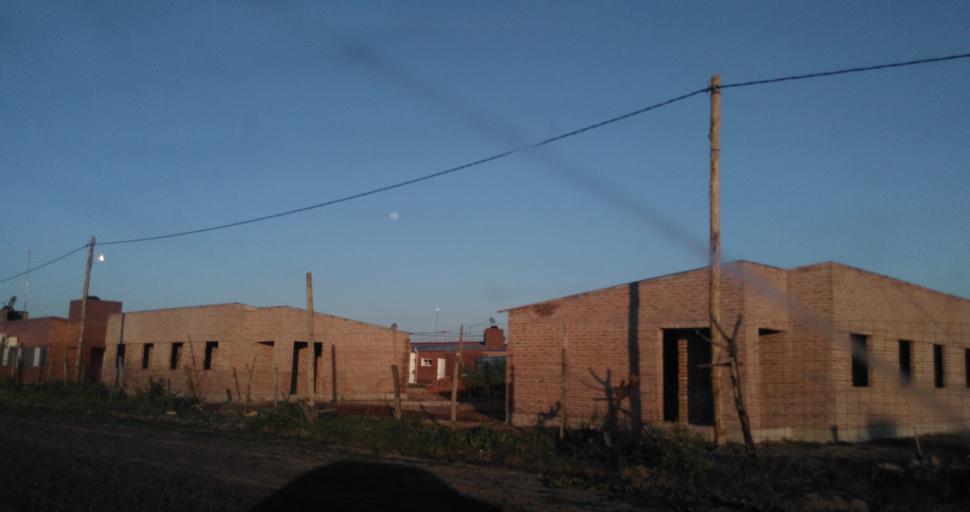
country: AR
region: Chaco
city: Resistencia
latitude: -27.4838
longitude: -59.0141
